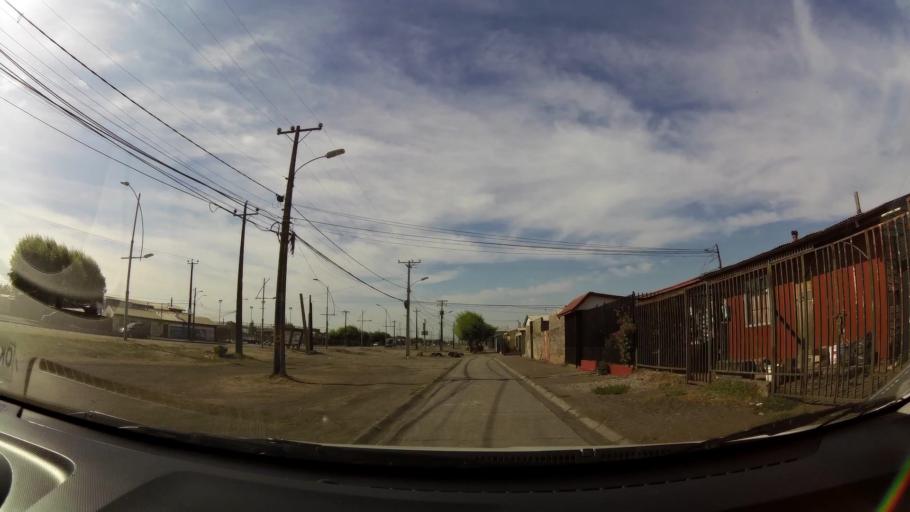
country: CL
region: Biobio
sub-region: Provincia de Concepcion
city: Talcahuano
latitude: -36.7776
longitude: -73.1131
